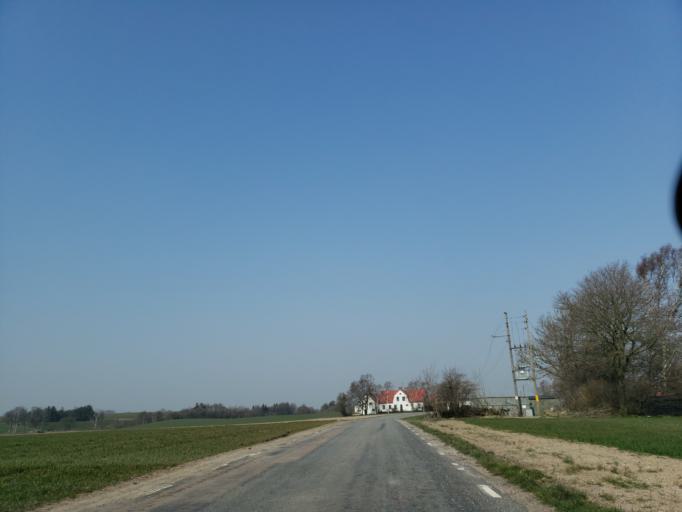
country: SE
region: Skane
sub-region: Simrishamns Kommun
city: Simrishamn
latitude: 55.4903
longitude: 14.2240
